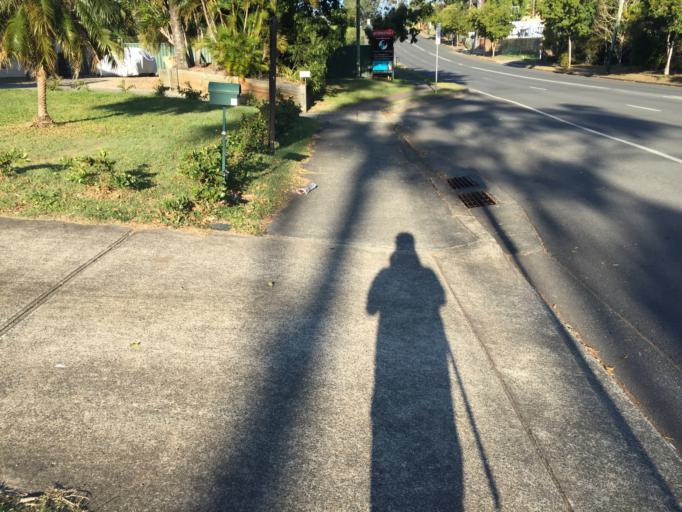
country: AU
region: Queensland
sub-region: Logan
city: Slacks Creek
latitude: -27.6356
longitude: 153.1523
